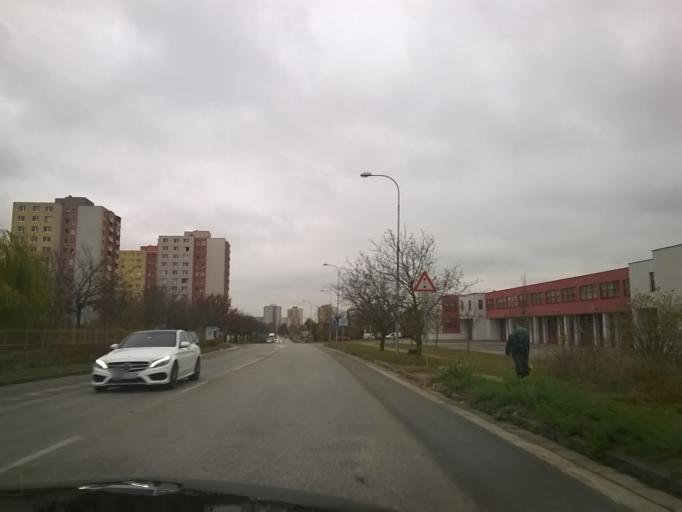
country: SK
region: Nitriansky
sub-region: Okres Nitra
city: Nitra
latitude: 48.2984
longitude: 18.0673
